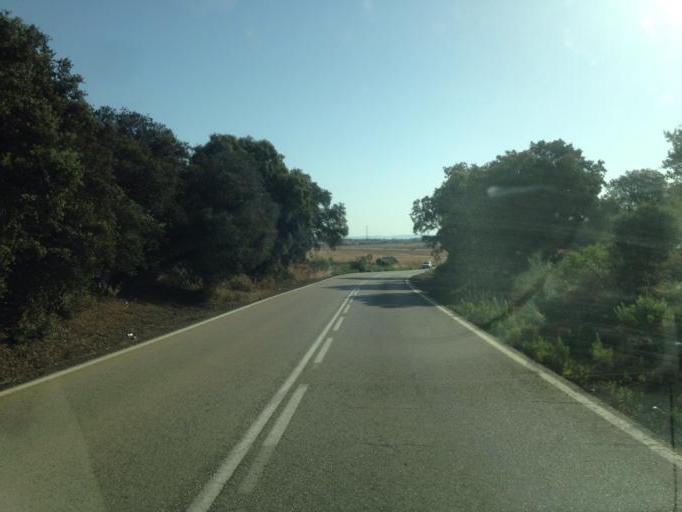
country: ES
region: Andalusia
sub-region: Provincia de Malaga
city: Villanueva de Tapia
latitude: 37.1173
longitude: -4.3128
